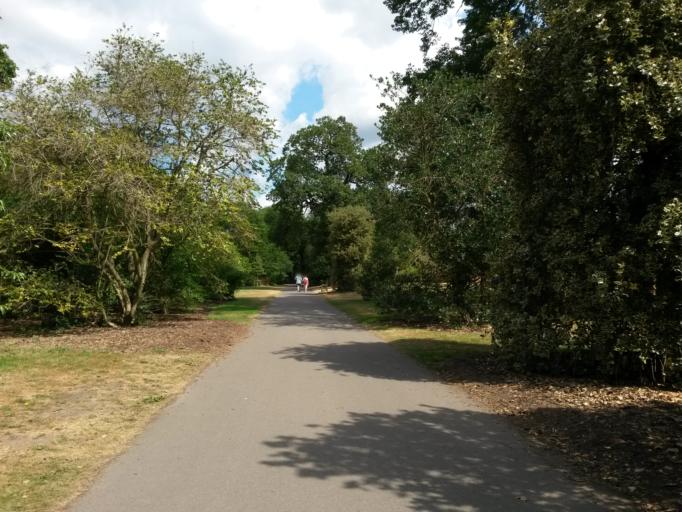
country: GB
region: England
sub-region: Greater London
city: Brentford
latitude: 51.4763
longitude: -0.2962
